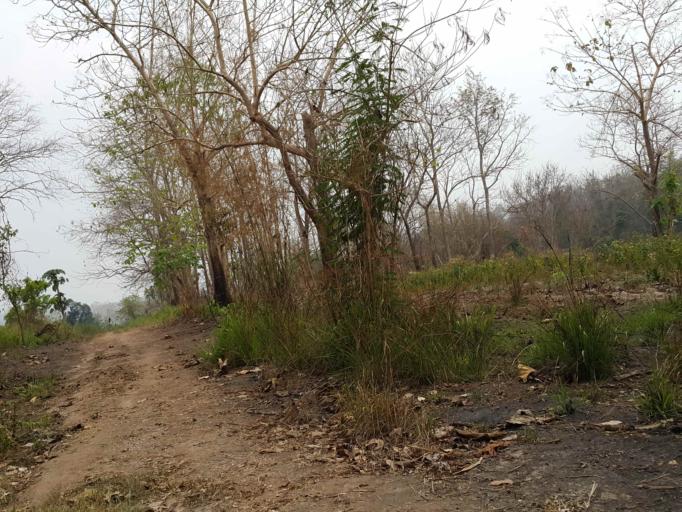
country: TH
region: Chiang Mai
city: Mae Taeng
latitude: 19.1165
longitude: 98.9881
